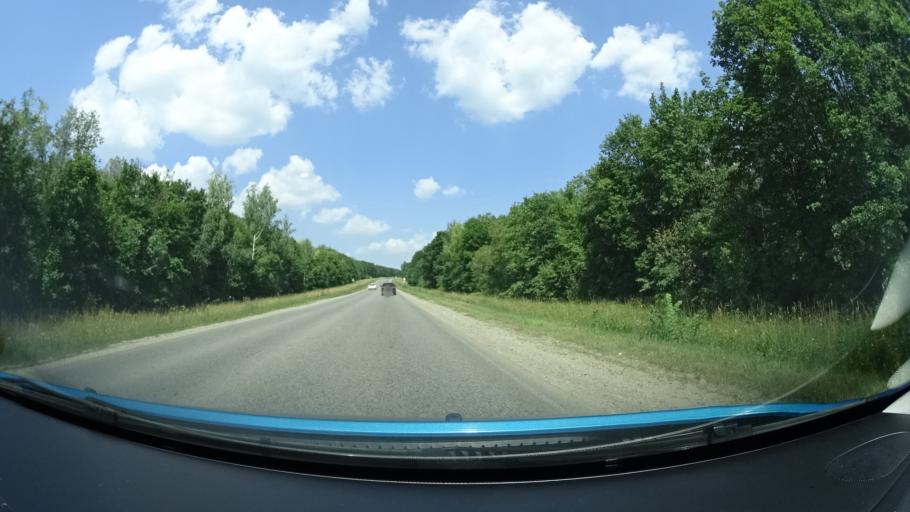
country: RU
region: Bashkortostan
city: Oktyabr'skiy
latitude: 54.4640
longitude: 53.5751
